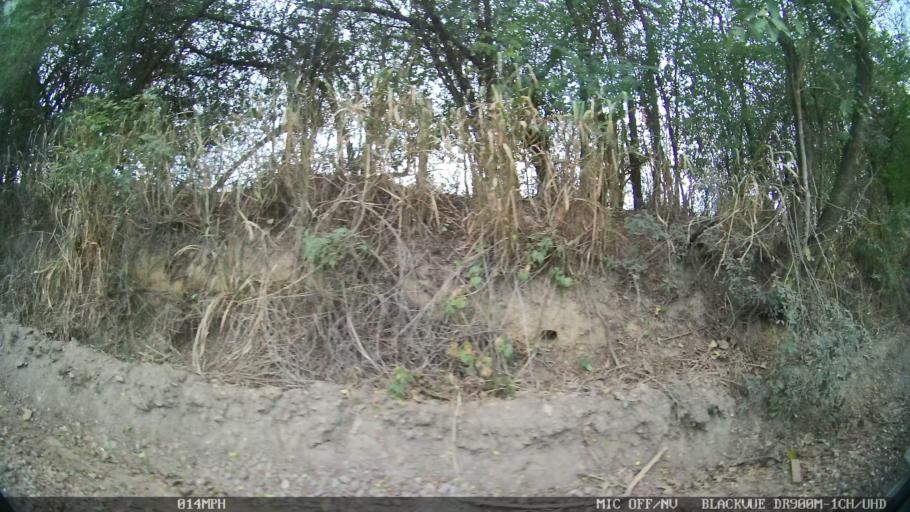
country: BR
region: Sao Paulo
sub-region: Americana
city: Americana
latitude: -22.6744
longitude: -47.3732
